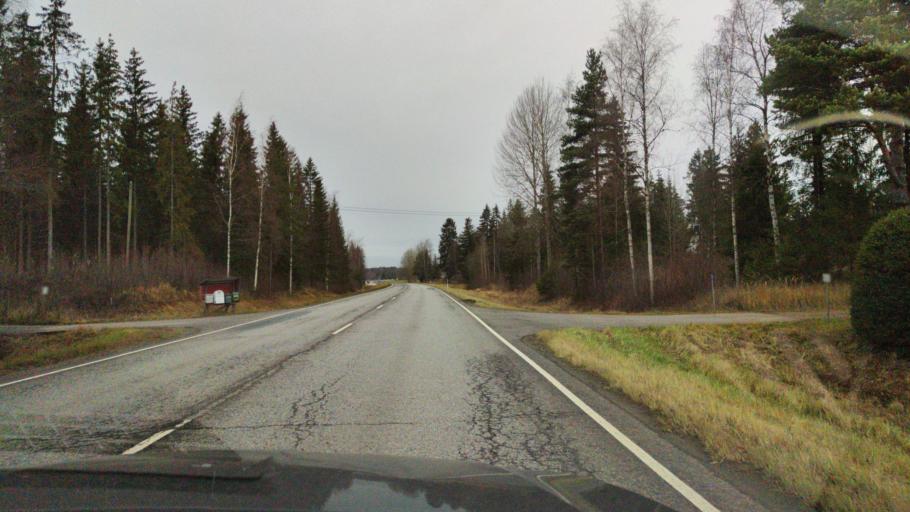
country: FI
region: Varsinais-Suomi
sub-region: Loimaa
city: Ylaene
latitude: 60.8673
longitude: 22.4081
